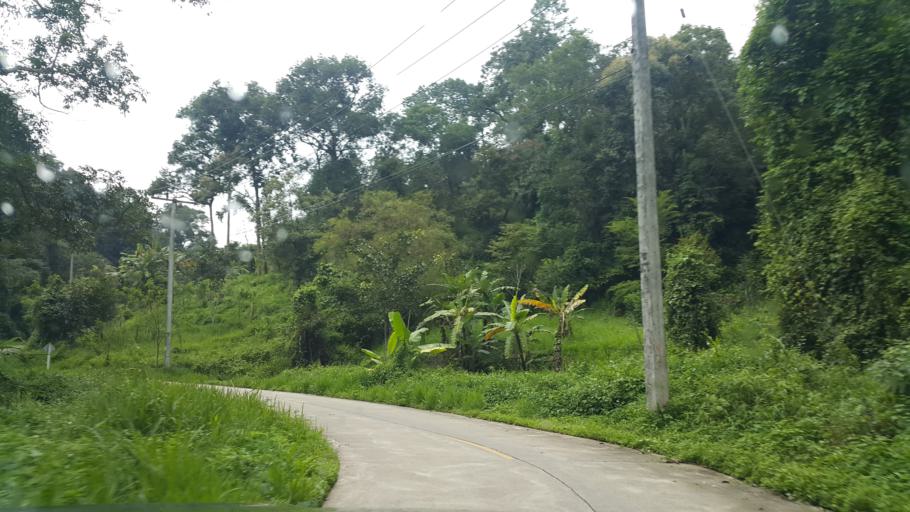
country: TH
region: Lampang
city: Wang Nuea
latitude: 19.0776
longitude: 99.3870
